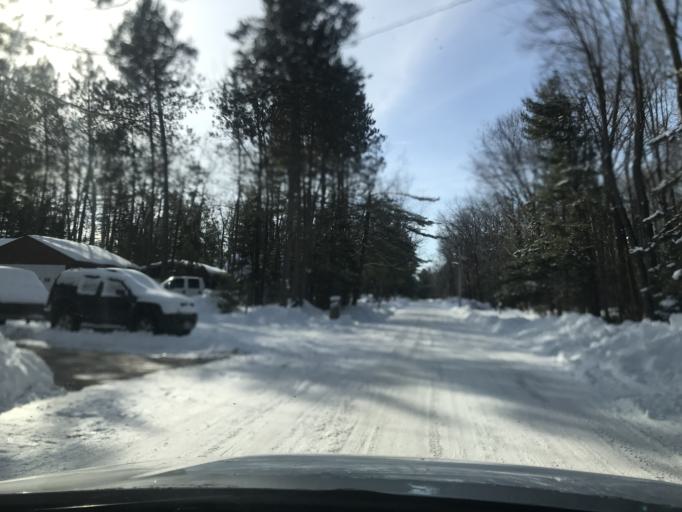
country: US
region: Wisconsin
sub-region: Oconto County
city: Gillett
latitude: 45.1529
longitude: -88.2152
